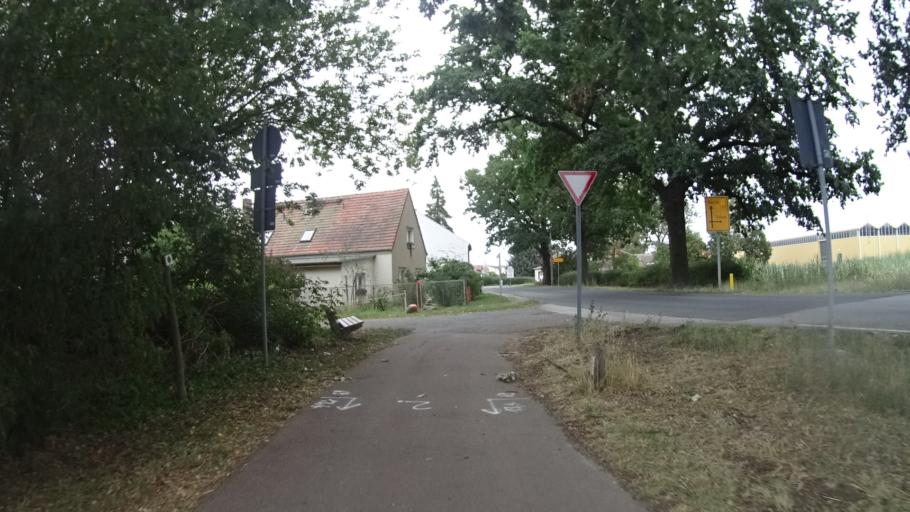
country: DE
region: Brandenburg
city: Baruth
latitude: 52.0500
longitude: 13.4671
